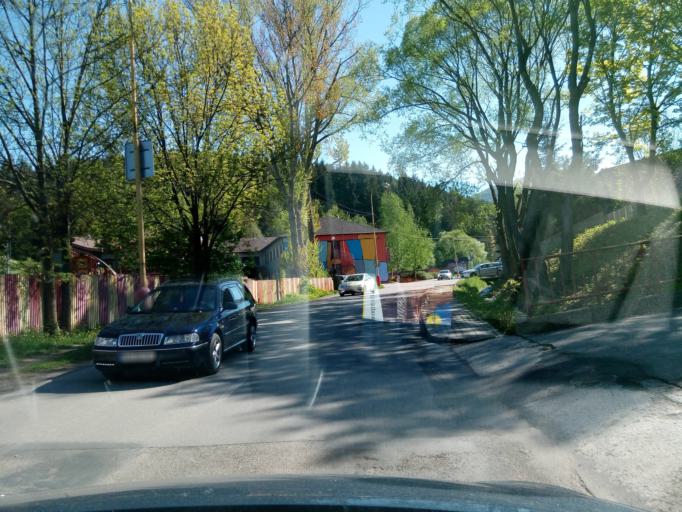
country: SK
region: Zilinsky
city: Ruzomberok
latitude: 49.0827
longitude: 19.2818
